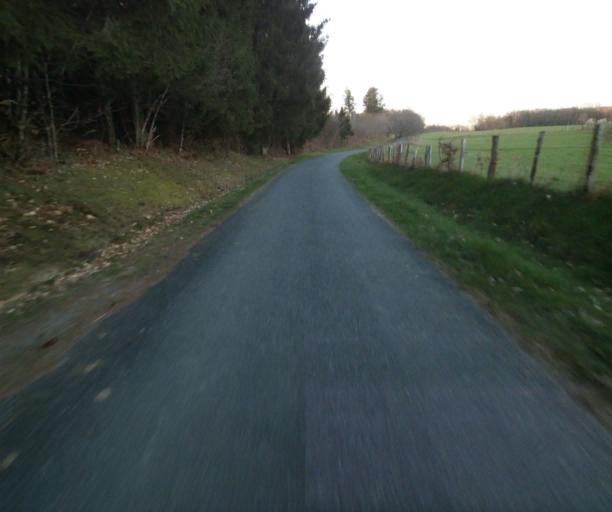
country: FR
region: Limousin
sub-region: Departement de la Correze
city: Uzerche
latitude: 45.3772
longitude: 1.6052
